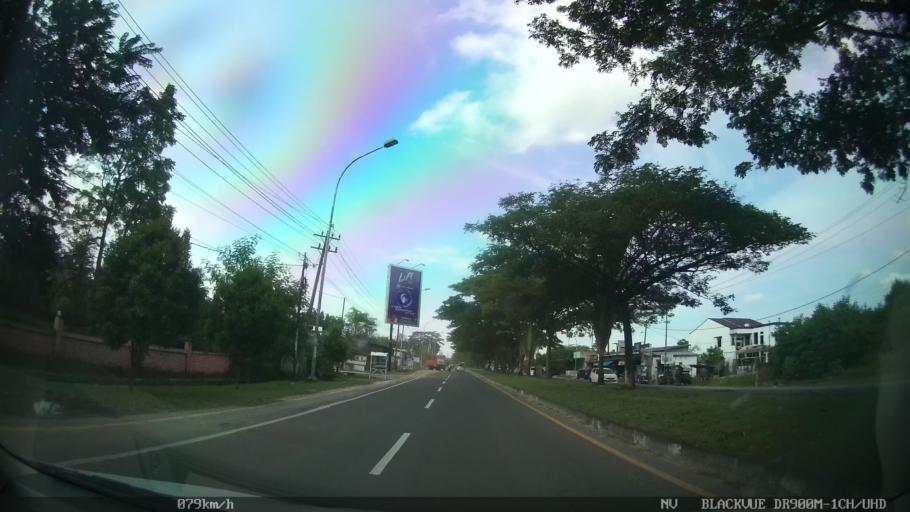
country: ID
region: North Sumatra
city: Percut
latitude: 3.5715
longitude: 98.7980
